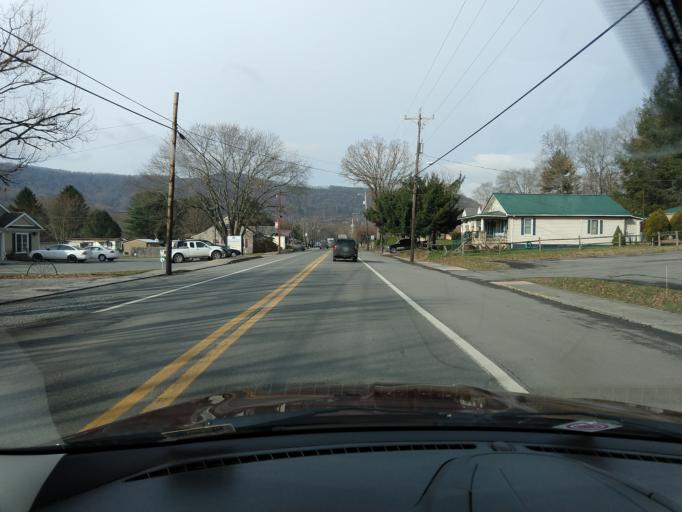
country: US
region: West Virginia
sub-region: Greenbrier County
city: Rainelle
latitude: 37.9638
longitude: -80.6933
